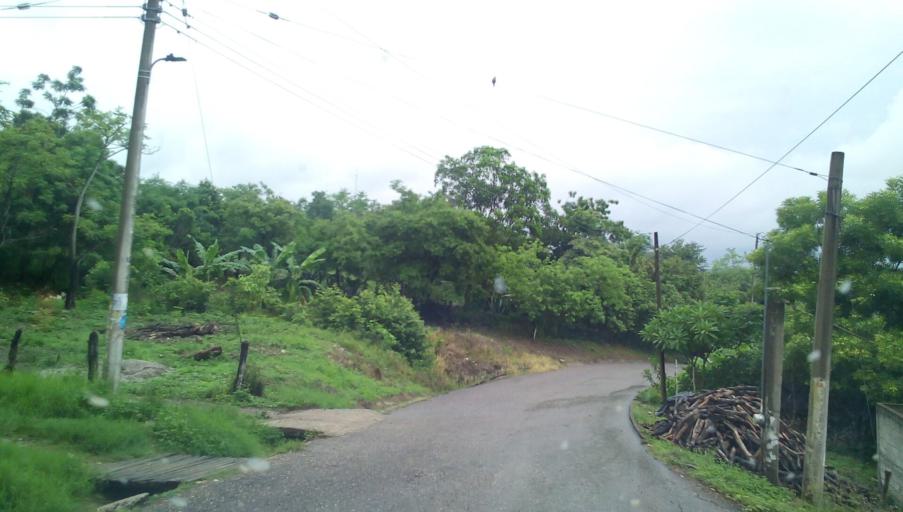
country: MX
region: Veracruz
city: Tempoal de Sanchez
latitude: 21.4614
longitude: -98.4259
